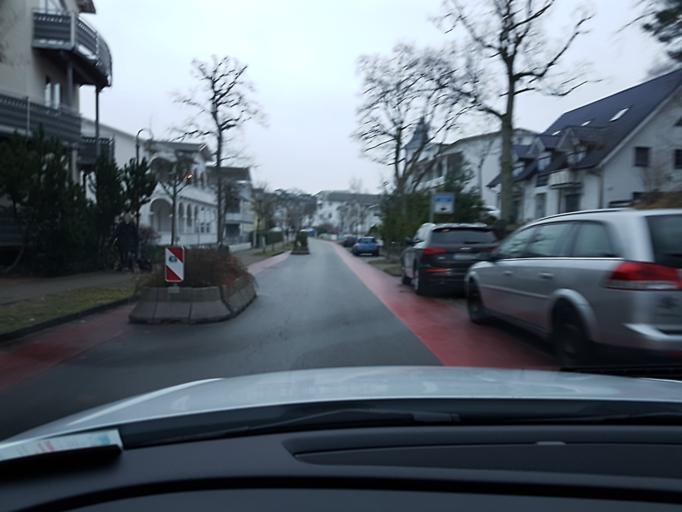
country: DE
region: Mecklenburg-Vorpommern
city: Ostseebad Binz
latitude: 54.4036
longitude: 13.6074
